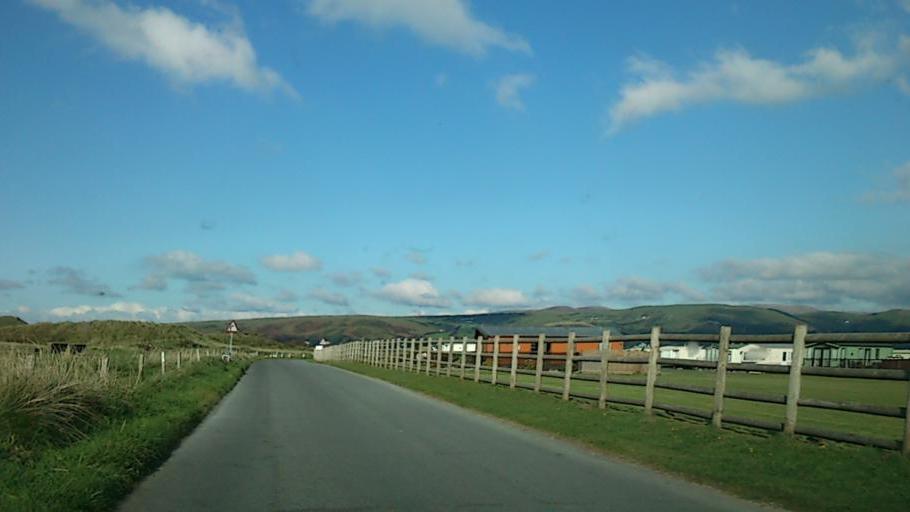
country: GB
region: Wales
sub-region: Gwynedd
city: Tywyn
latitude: 52.5199
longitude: -4.0537
